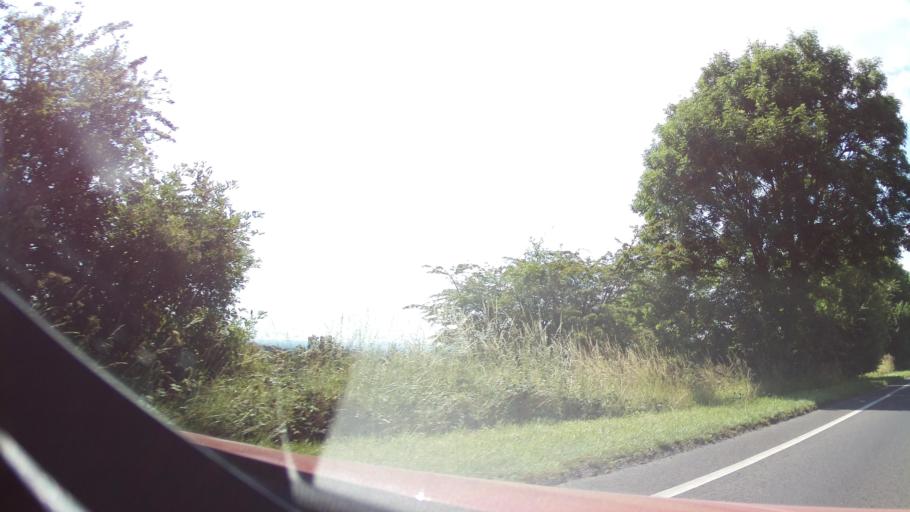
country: GB
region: England
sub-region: Worcestershire
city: Barnt Green
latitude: 52.3240
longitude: -2.0081
